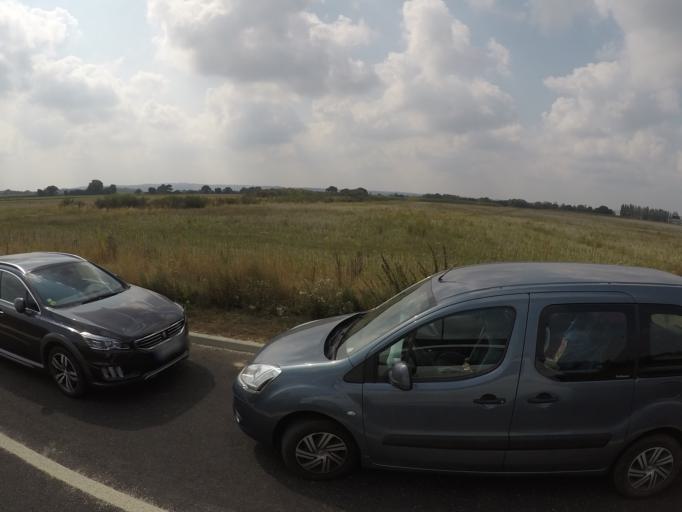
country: FR
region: Brittany
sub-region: Departement des Cotes-d'Armor
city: Plelo
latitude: 48.5302
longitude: -2.9355
